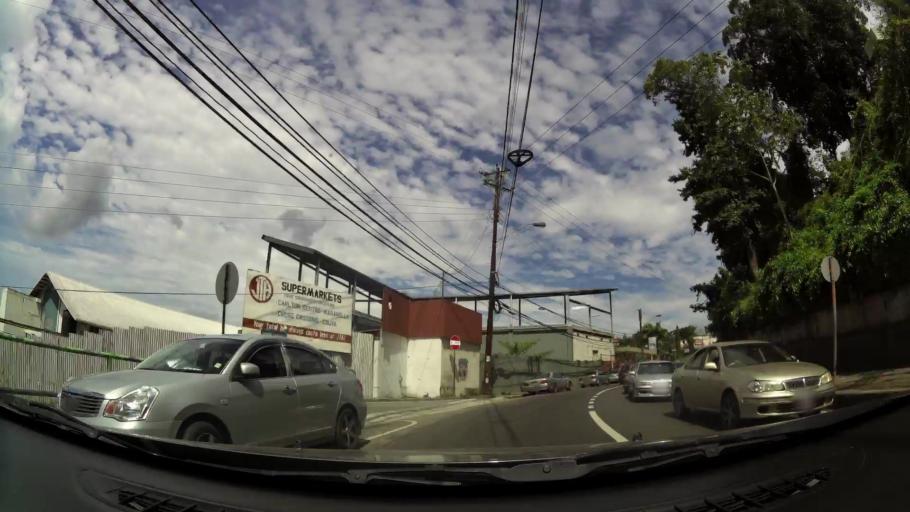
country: TT
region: City of San Fernando
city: San Fernando
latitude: 10.2815
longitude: -61.4626
